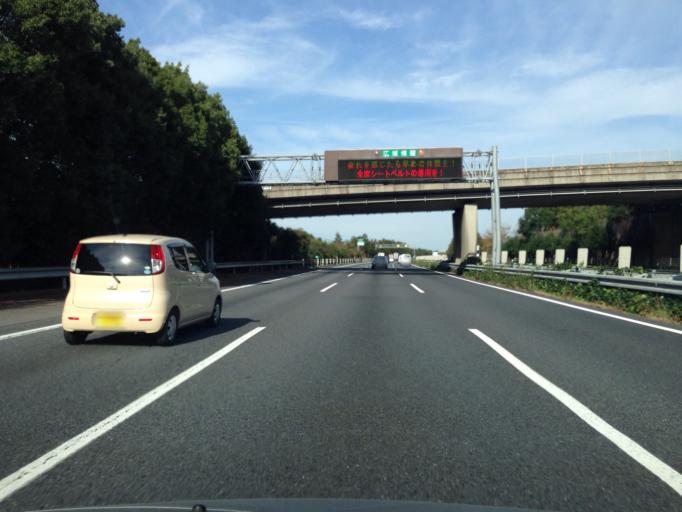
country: JP
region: Ibaraki
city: Ishioka
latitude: 36.2510
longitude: 140.2970
